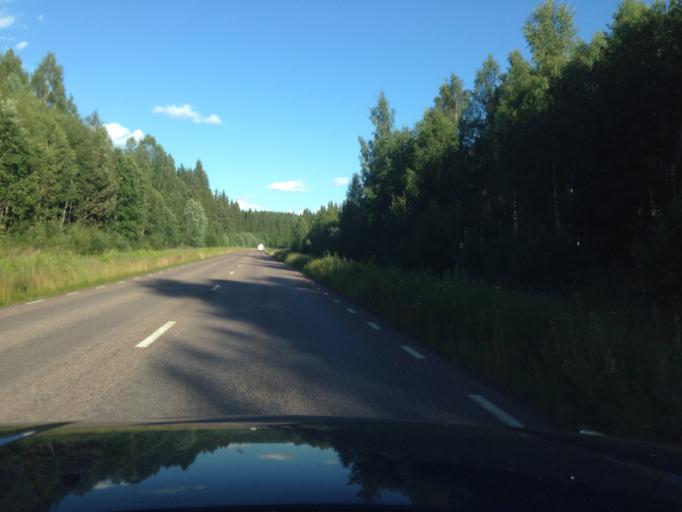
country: SE
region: Dalarna
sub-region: Ludvika Kommun
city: Ludvika
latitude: 60.1418
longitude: 15.1249
